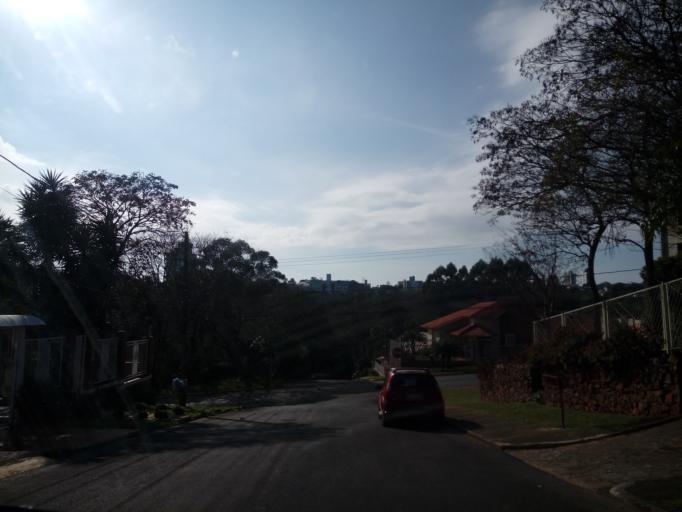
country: BR
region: Santa Catarina
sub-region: Chapeco
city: Chapeco
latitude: -27.1191
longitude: -52.6128
